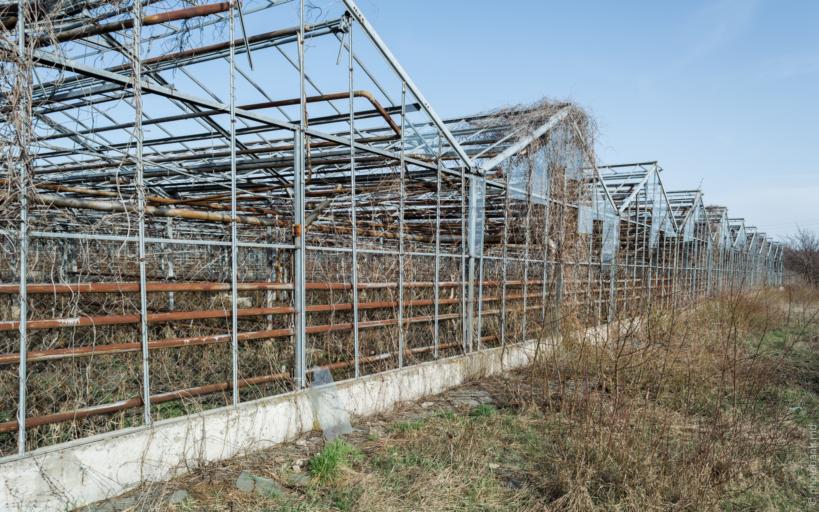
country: MD
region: Balti
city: Balti
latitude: 47.7665
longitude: 27.8943
